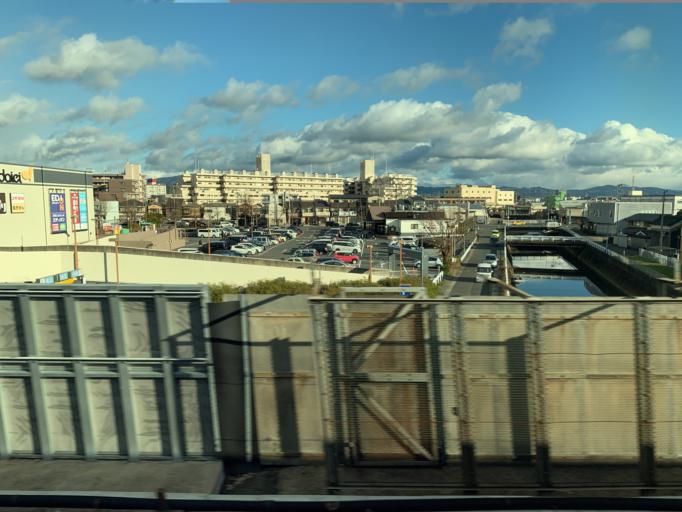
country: JP
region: Kyoto
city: Muko
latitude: 34.9659
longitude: 135.7162
